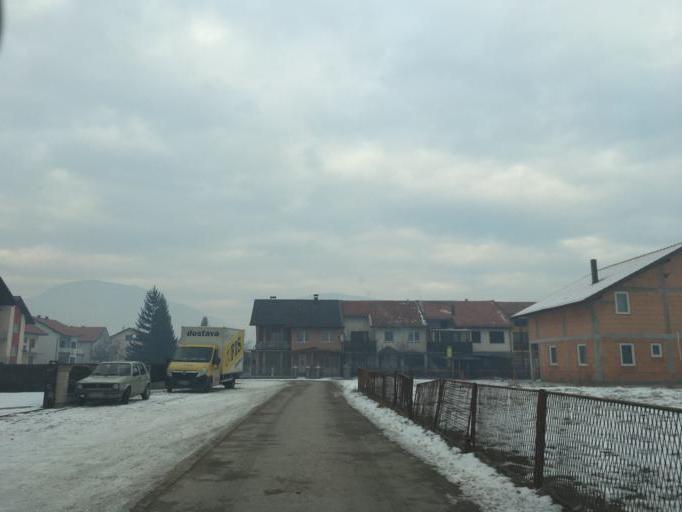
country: BA
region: Federation of Bosnia and Herzegovina
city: Bugojno
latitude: 44.0599
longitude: 17.4528
